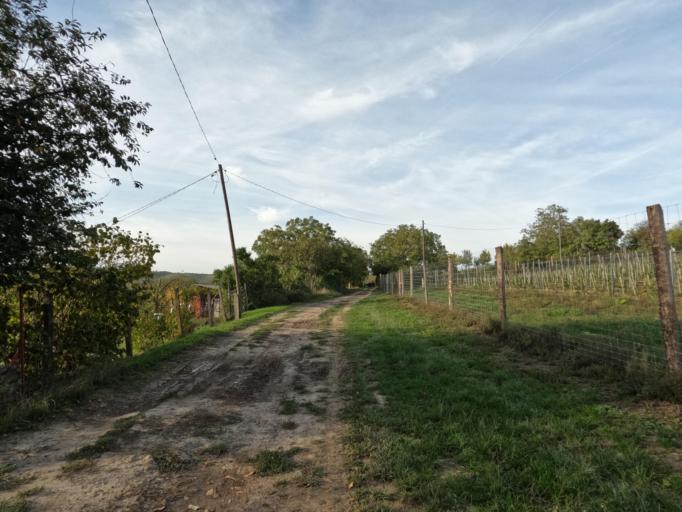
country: HU
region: Tolna
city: Szekszard
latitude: 46.3278
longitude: 18.6722
